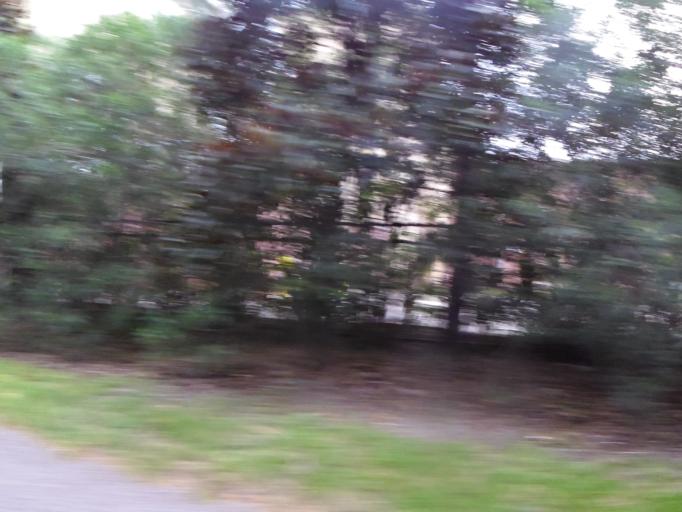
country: US
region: Florida
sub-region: Duval County
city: Jacksonville
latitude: 30.3510
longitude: -81.6306
